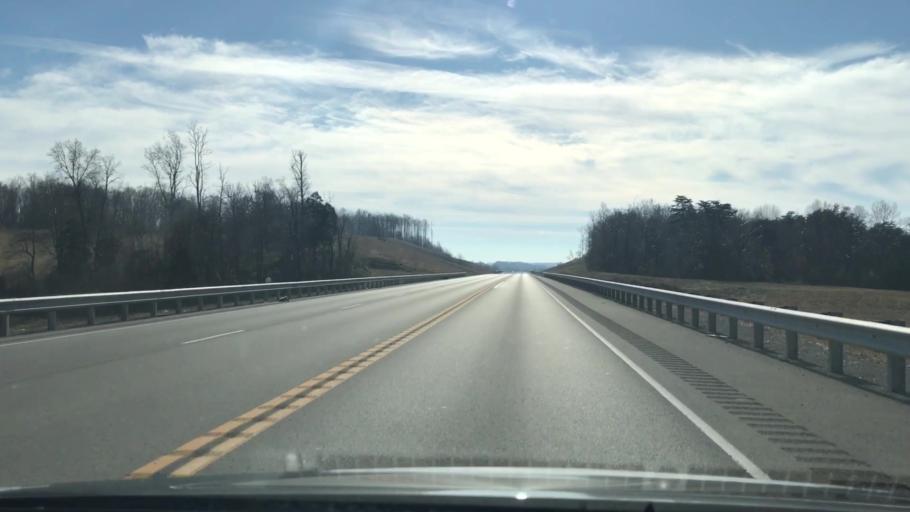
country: US
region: Kentucky
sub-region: Metcalfe County
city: Edmonton
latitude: 36.8536
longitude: -85.6742
